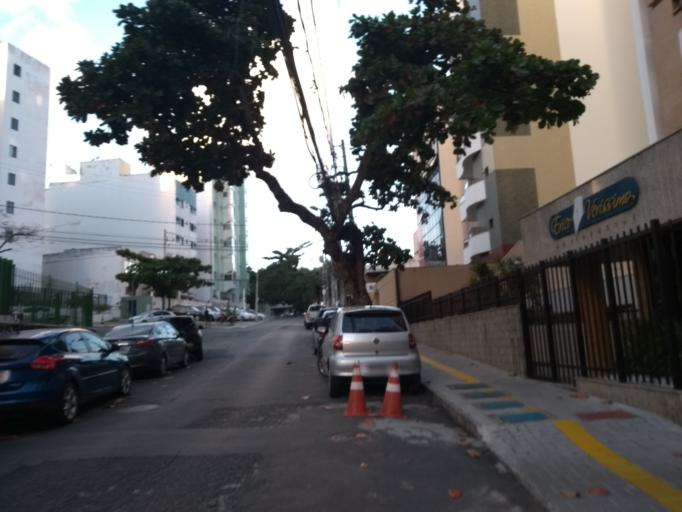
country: BR
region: Bahia
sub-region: Salvador
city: Salvador
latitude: -12.9978
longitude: -38.4607
